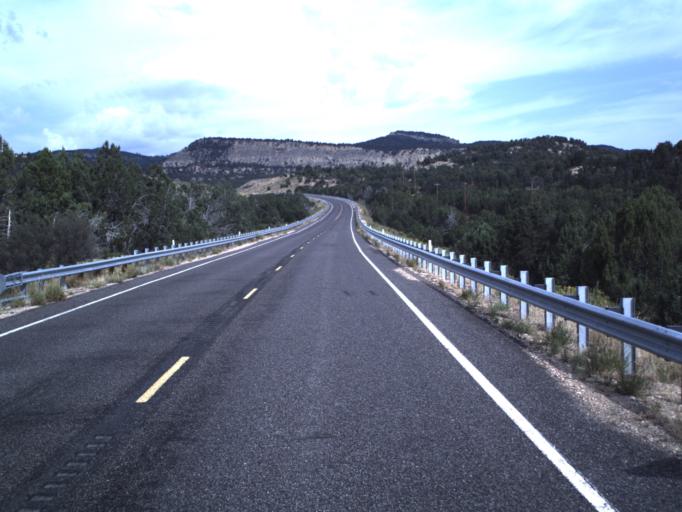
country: US
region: Utah
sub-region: Kane County
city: Kanab
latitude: 37.2547
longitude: -112.7639
